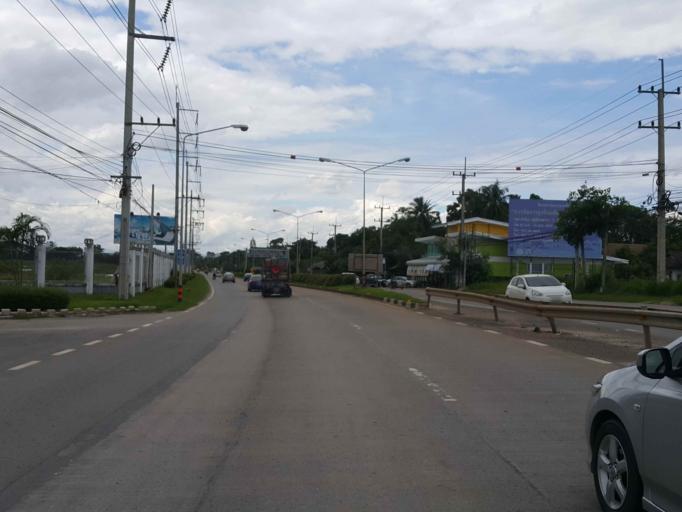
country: TH
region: Chiang Mai
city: San Sai
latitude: 18.8775
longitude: 98.9619
